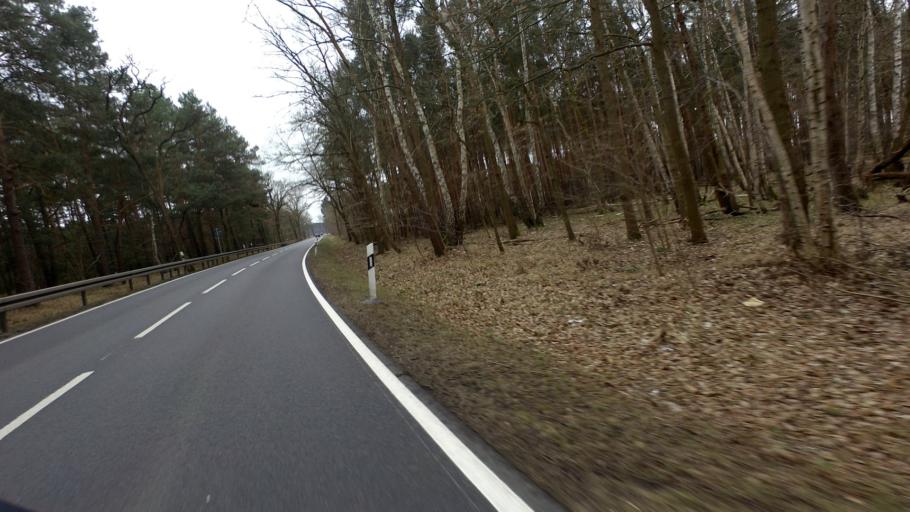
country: DE
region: Brandenburg
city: Luckenwalde
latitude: 52.1227
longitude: 13.2183
